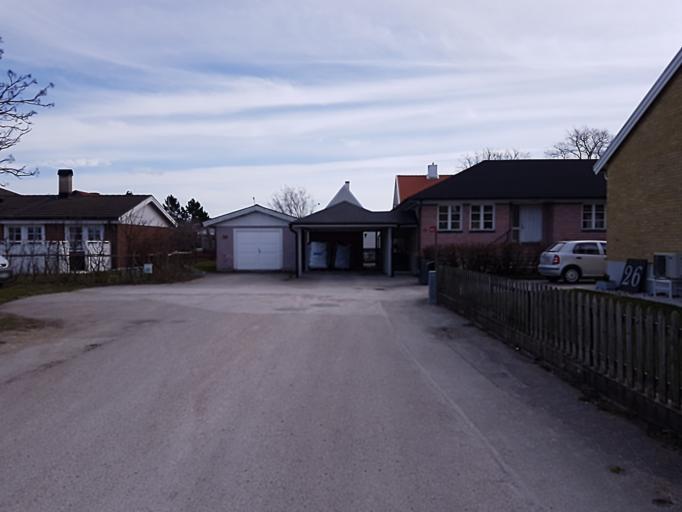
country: SE
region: Gotland
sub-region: Gotland
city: Visby
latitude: 57.6344
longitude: 18.3188
